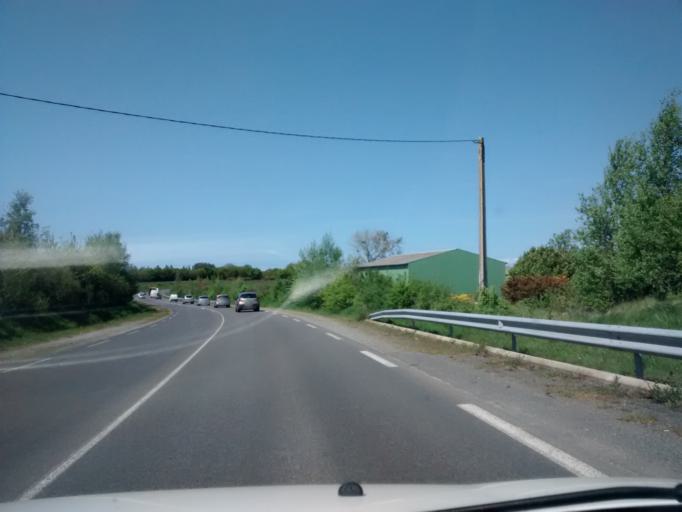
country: FR
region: Brittany
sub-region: Departement d'Ille-et-Vilaine
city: Pleurtuit
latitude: 48.5951
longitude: -2.0687
